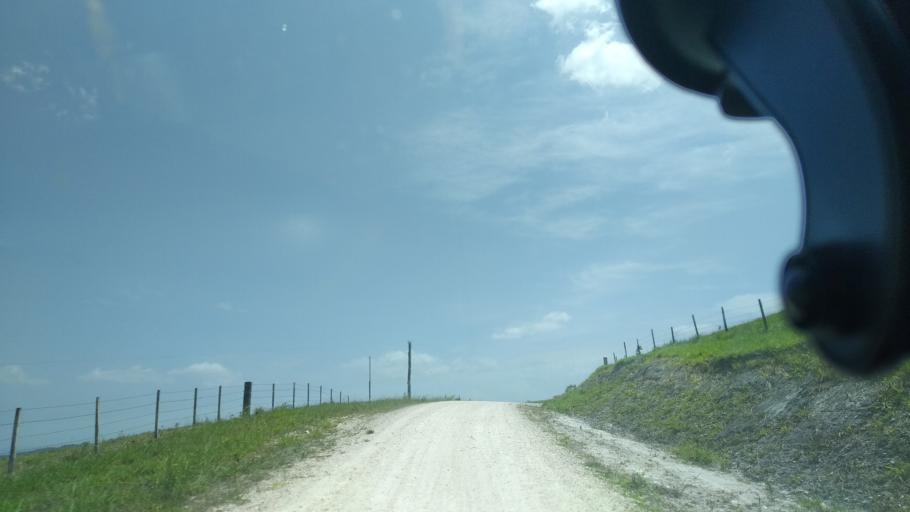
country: BZ
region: Cayo
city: San Ignacio
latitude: 17.2997
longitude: -89.0575
